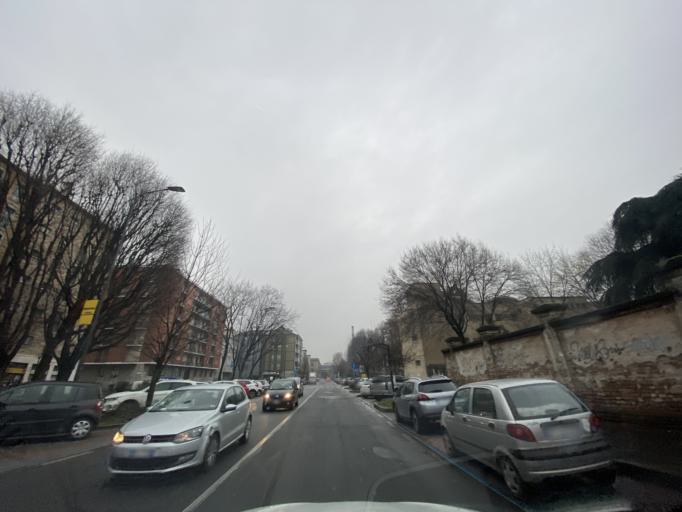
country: IT
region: Lombardy
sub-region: Citta metropolitana di Milano
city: Milano
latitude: 45.4991
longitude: 9.1784
